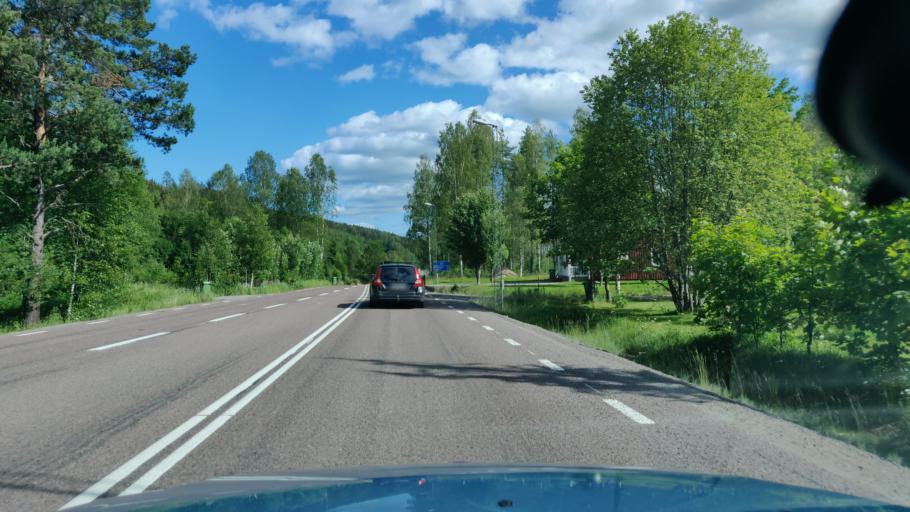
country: SE
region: Vaermland
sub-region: Torsby Kommun
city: Torsby
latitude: 60.6753
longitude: 12.9483
